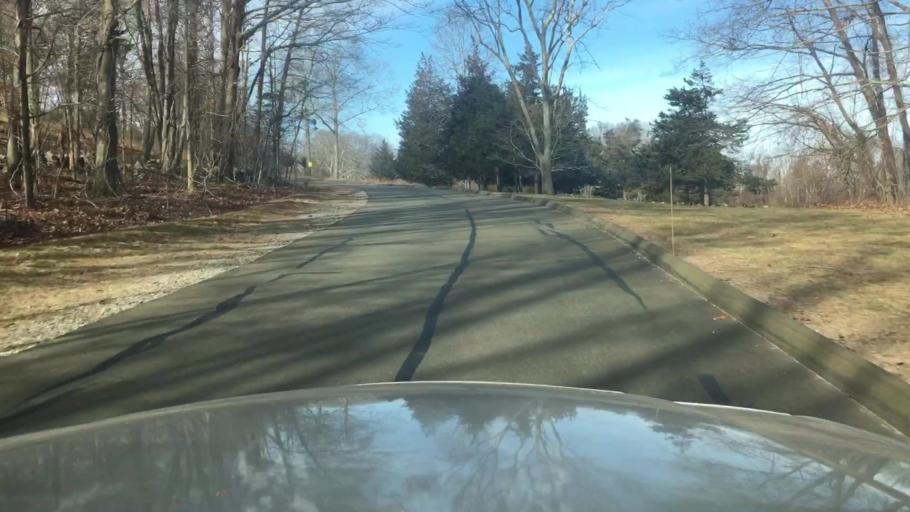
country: US
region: Connecticut
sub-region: Middlesex County
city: Essex Village
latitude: 41.3757
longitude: -72.3901
